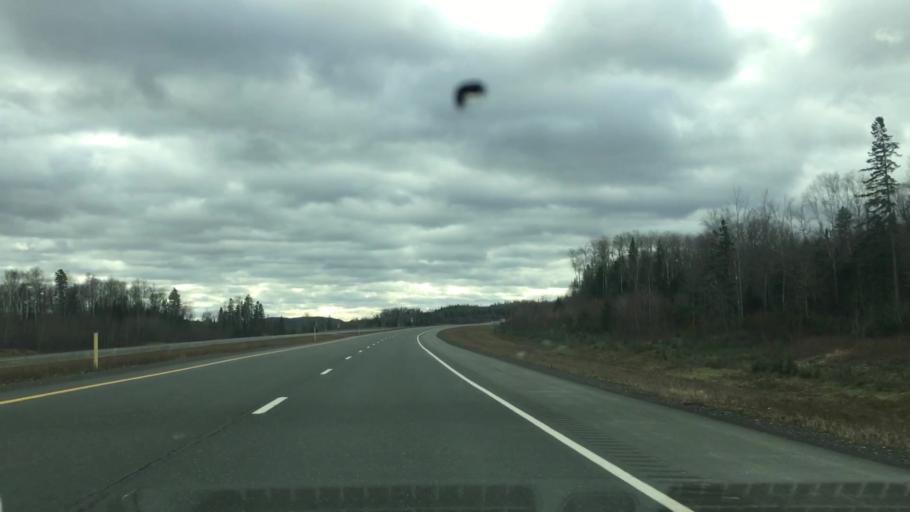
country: US
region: Maine
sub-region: Aroostook County
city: Fort Fairfield
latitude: 46.6740
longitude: -67.7300
